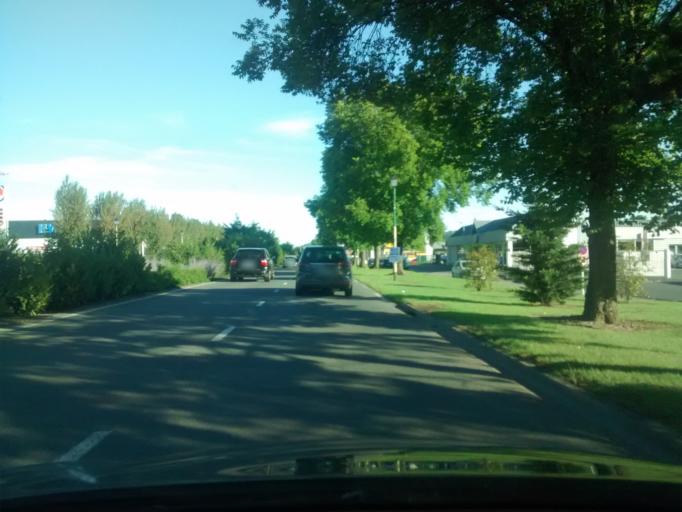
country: FR
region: Lower Normandy
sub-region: Departement du Calvados
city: Touques
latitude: 49.3442
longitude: 0.0998
